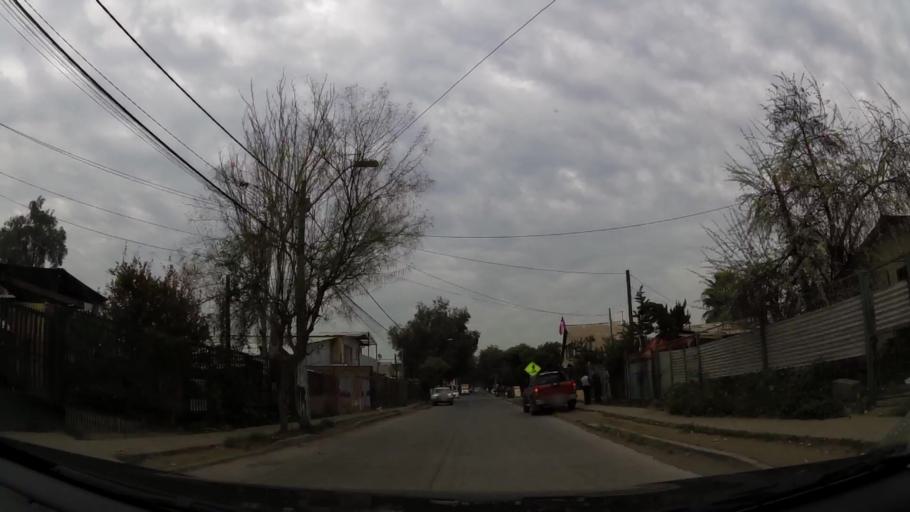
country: CL
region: Santiago Metropolitan
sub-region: Provincia de Chacabuco
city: Lampa
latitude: -33.2279
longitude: -70.8080
